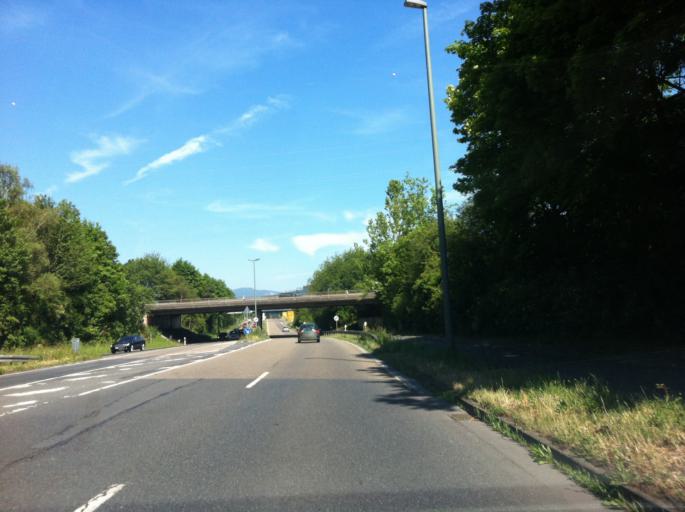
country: DE
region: Hesse
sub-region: Regierungsbezirk Darmstadt
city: Eschborn
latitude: 50.1332
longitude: 8.5867
